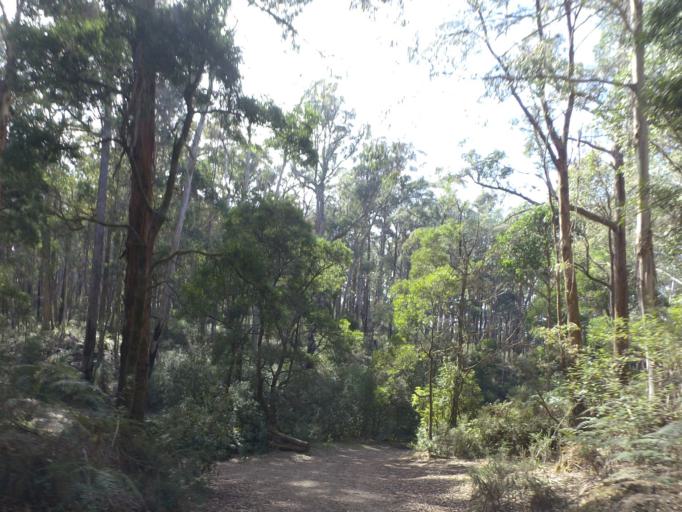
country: AU
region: Victoria
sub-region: Moorabool
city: Bacchus Marsh
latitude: -37.4530
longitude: 144.2624
